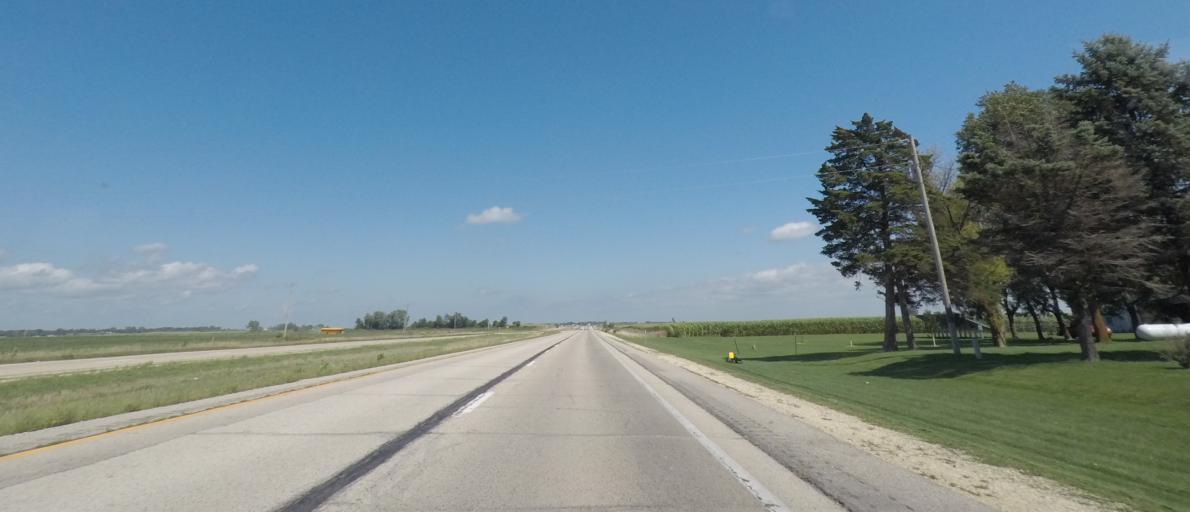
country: US
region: Iowa
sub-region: Linn County
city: Springville
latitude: 42.0670
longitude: -91.3831
